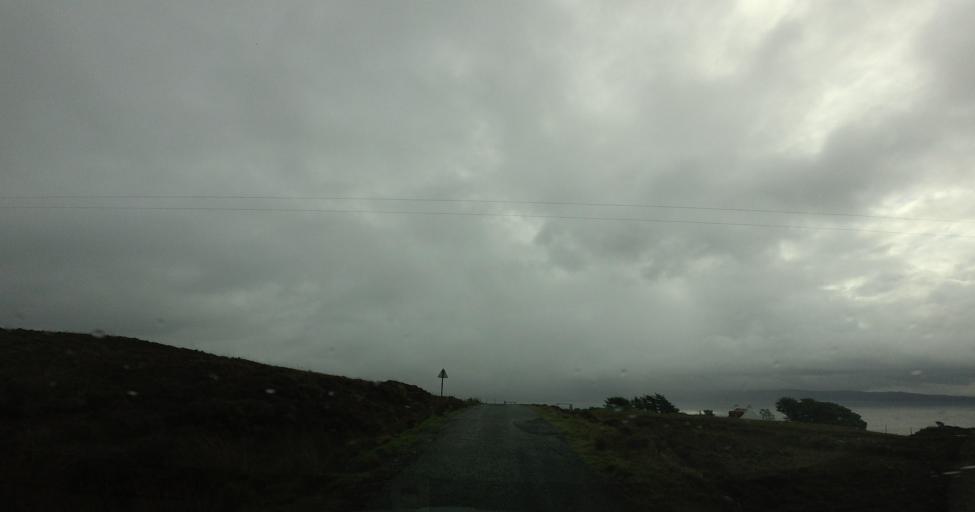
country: GB
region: Scotland
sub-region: Highland
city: Isle of Skye
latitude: 57.1425
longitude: -6.0739
